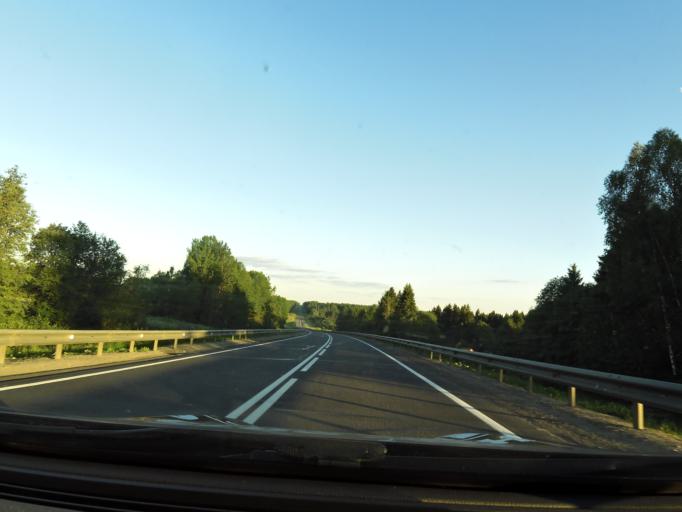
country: RU
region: Vologda
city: Gryazovets
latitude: 58.7015
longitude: 40.2977
